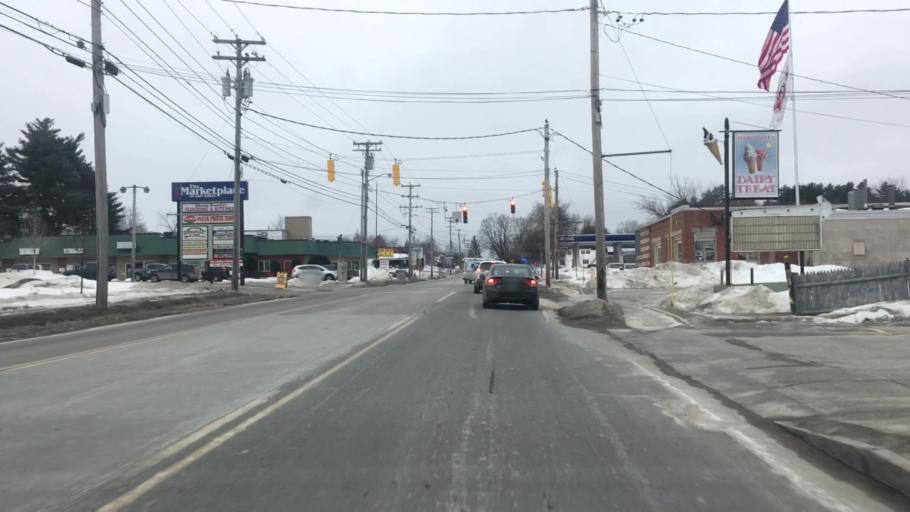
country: US
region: Maine
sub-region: Androscoggin County
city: Lewiston
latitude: 44.1214
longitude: -70.2027
